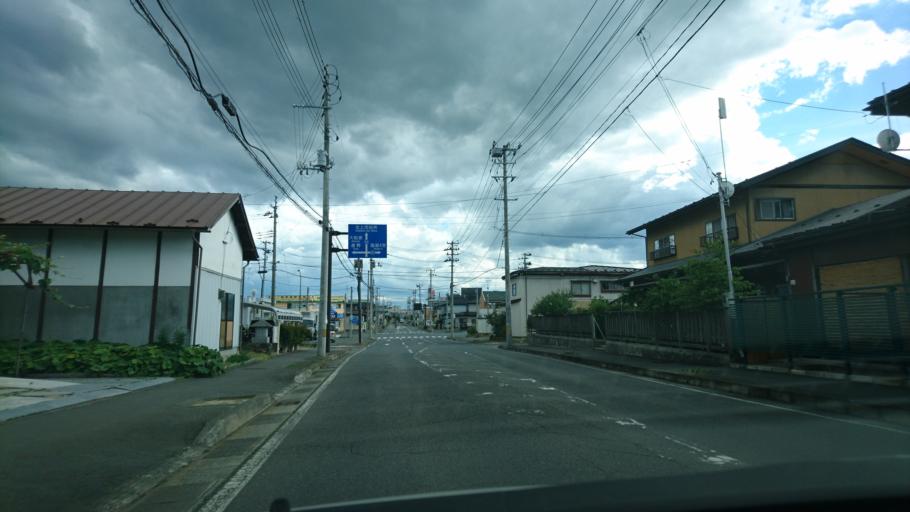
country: JP
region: Iwate
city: Kitakami
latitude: 39.2954
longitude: 141.1214
